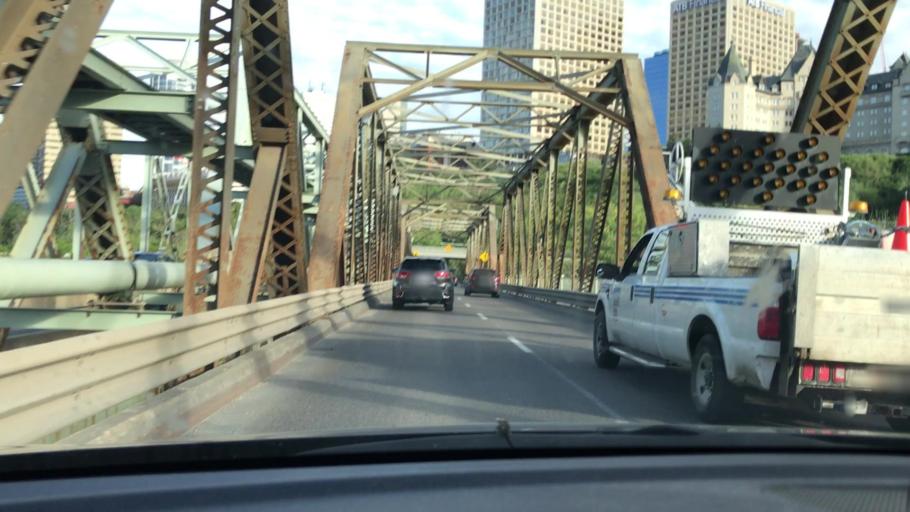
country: CA
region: Alberta
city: Edmonton
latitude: 53.5380
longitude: -113.4871
